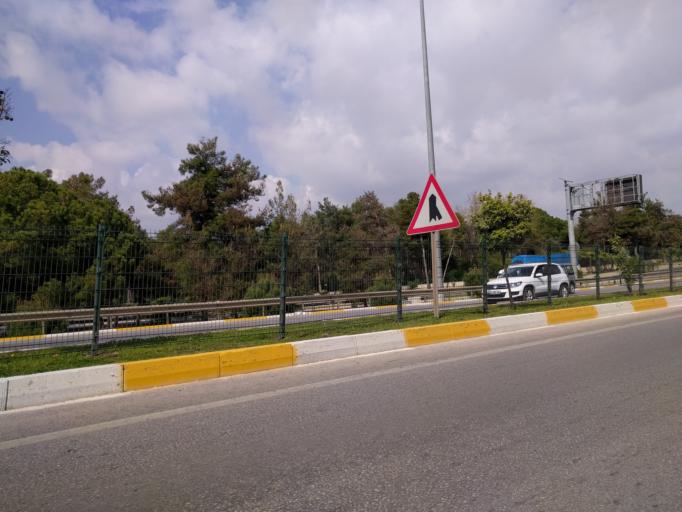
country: TR
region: Antalya
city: Antalya
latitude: 36.9016
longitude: 30.6666
